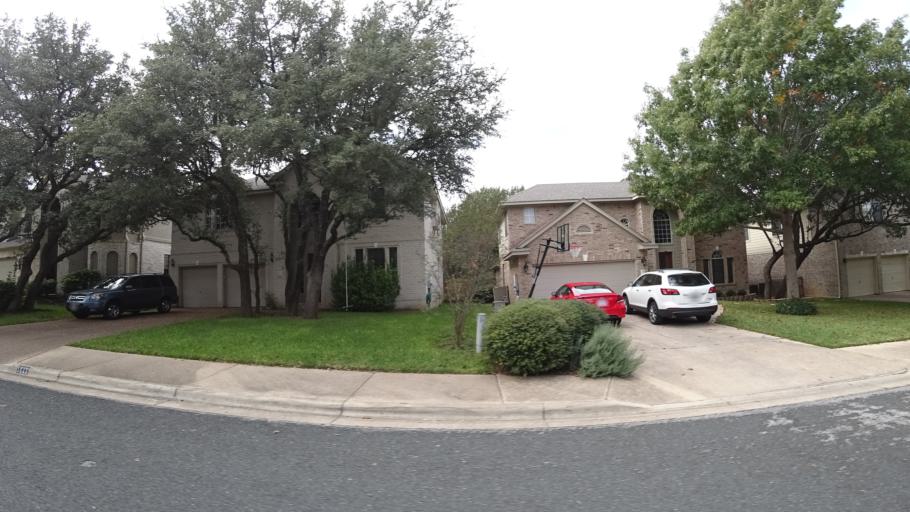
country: US
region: Texas
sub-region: Williamson County
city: Brushy Creek
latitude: 30.5166
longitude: -97.7383
